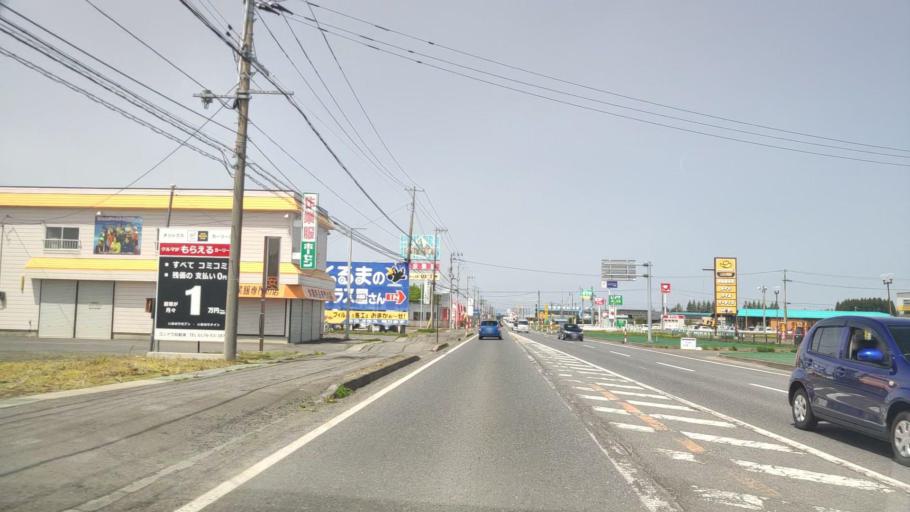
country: JP
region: Aomori
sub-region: Misawa Shi
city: Inuotose
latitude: 40.6449
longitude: 141.1986
